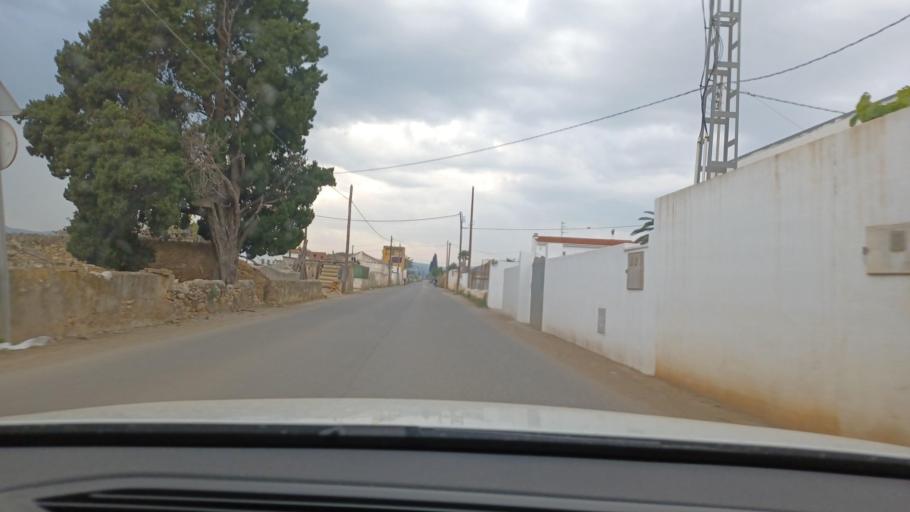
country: ES
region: Valencia
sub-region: Provincia de Castello
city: Benicarlo
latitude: 40.4029
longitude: 0.4098
